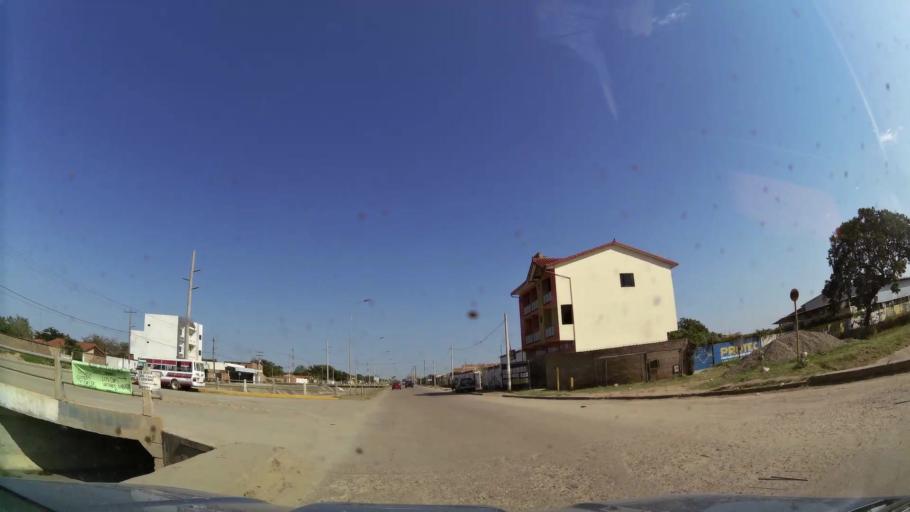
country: BO
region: Santa Cruz
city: Cotoca
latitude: -17.7865
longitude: -63.1082
